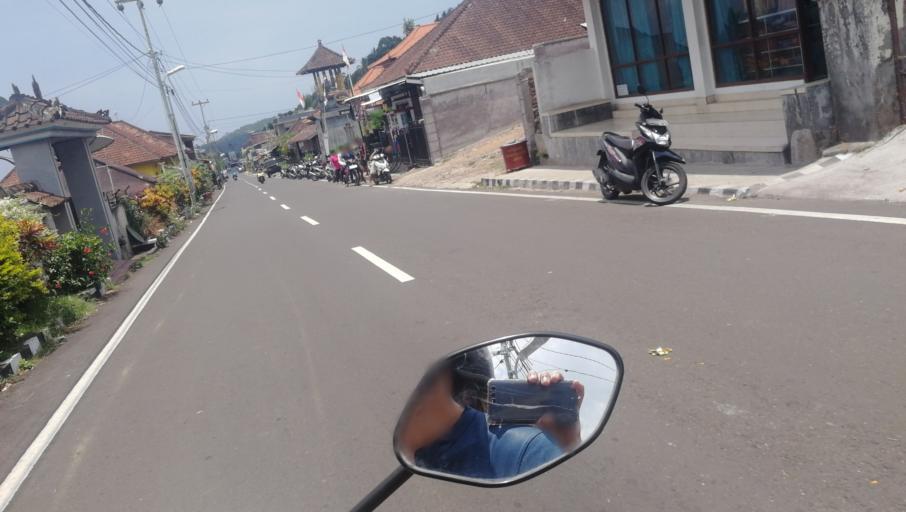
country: ID
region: Bali
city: Banjar Pedawa
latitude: -8.2628
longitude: 115.0319
